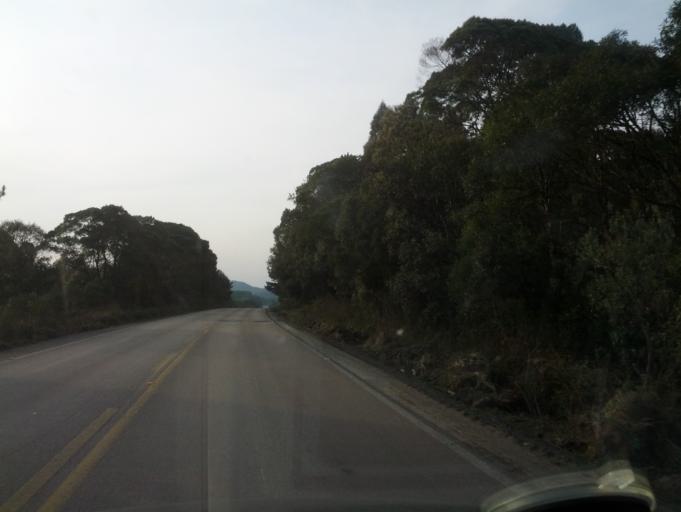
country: BR
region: Santa Catarina
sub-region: Otacilio Costa
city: Otacilio Costa
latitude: -27.3336
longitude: -50.1330
